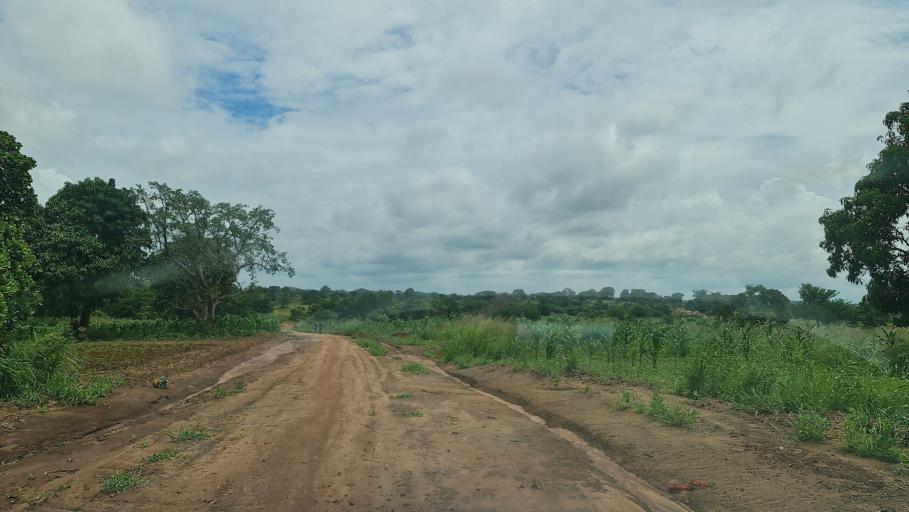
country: MZ
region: Cabo Delgado
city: Pemba
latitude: -13.5213
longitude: 40.0183
